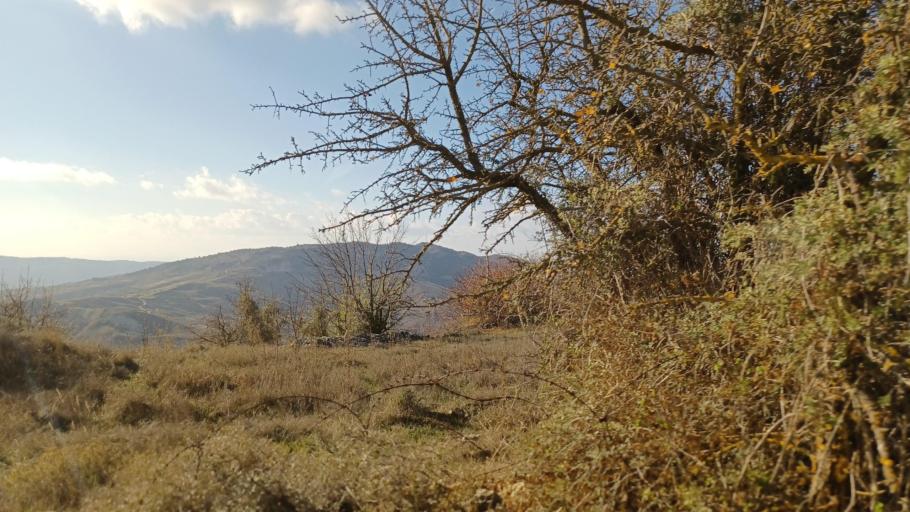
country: CY
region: Limassol
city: Pachna
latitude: 34.8393
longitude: 32.6823
